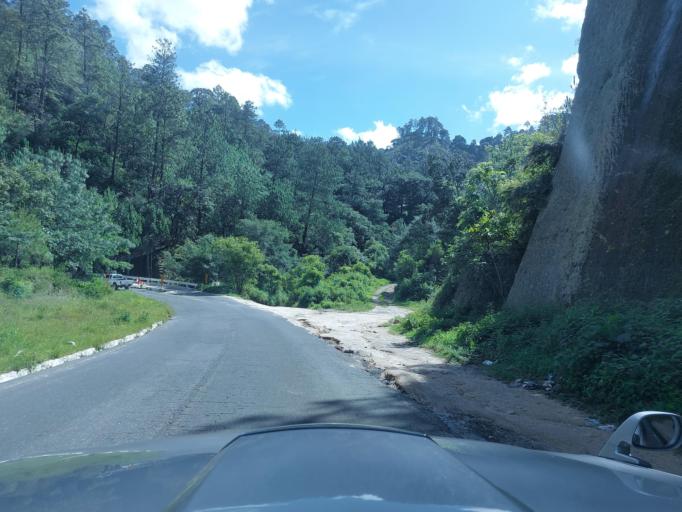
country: GT
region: Chimaltenango
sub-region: Municipio de Santa Cruz Balanya
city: Santa Cruz Balanya
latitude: 14.6958
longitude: -90.8953
